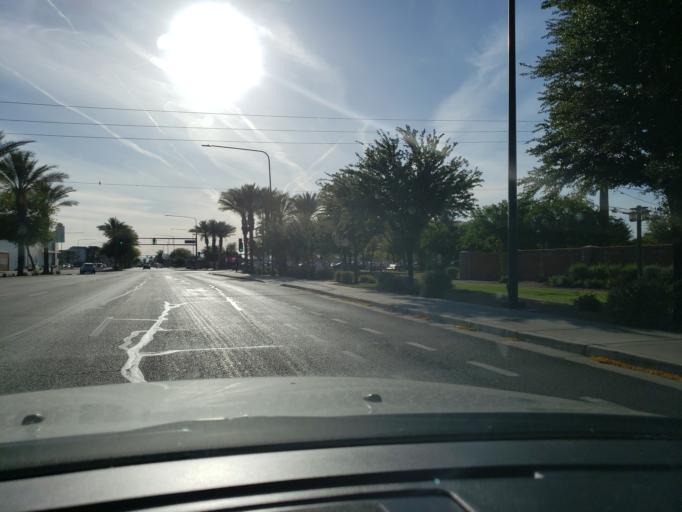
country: US
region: Arizona
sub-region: Maricopa County
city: Chandler
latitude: 33.3063
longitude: -111.8404
